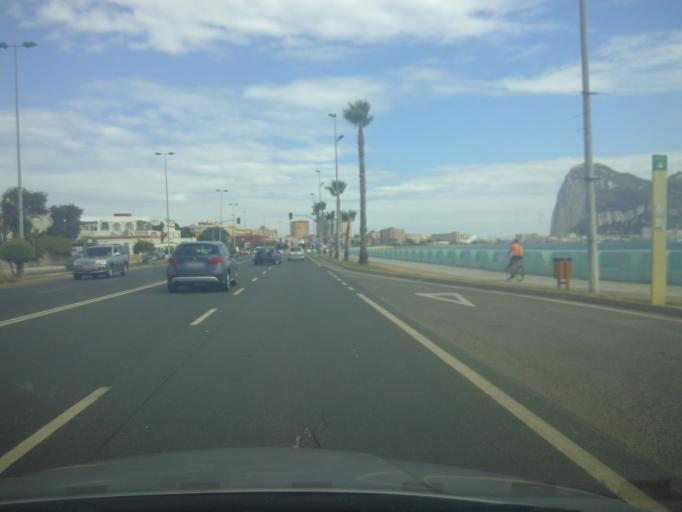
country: ES
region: Andalusia
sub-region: Provincia de Cadiz
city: La Linea de la Concepcion
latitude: 36.1676
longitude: -5.3665
